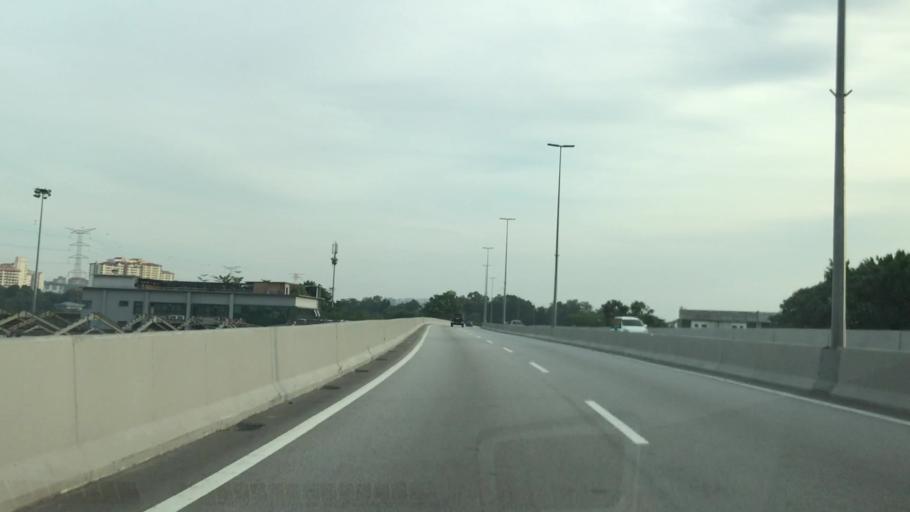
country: MY
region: Kuala Lumpur
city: Kuala Lumpur
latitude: 3.1133
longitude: 101.7129
